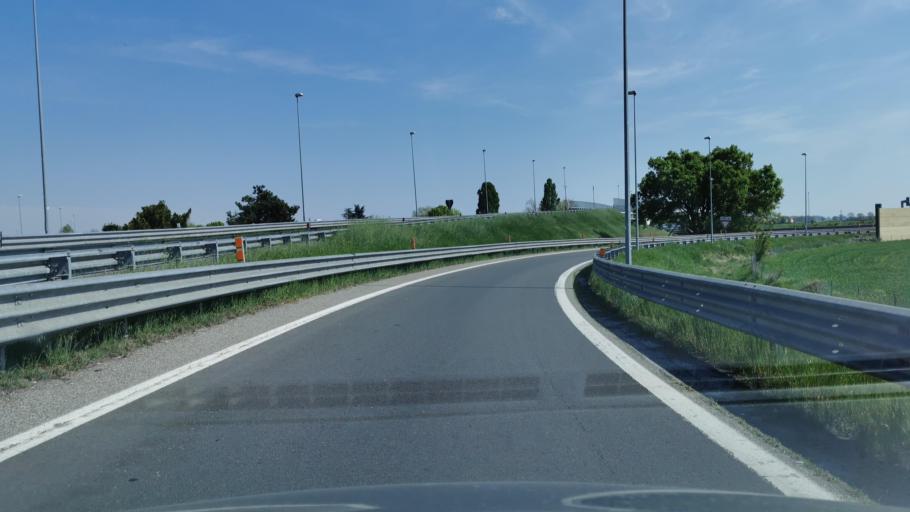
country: IT
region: Emilia-Romagna
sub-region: Provincia di Piacenza
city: Castelvetro Piacentino
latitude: 45.0893
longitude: 9.9957
